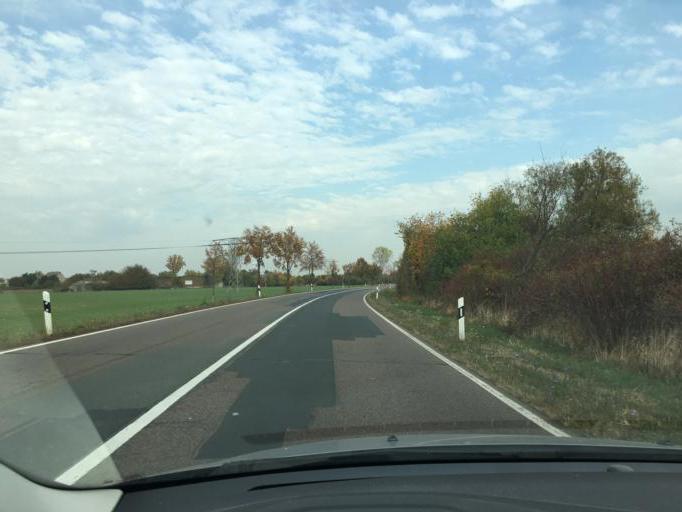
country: DE
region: Saxony
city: Zwochau
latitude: 51.4878
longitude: 12.2701
